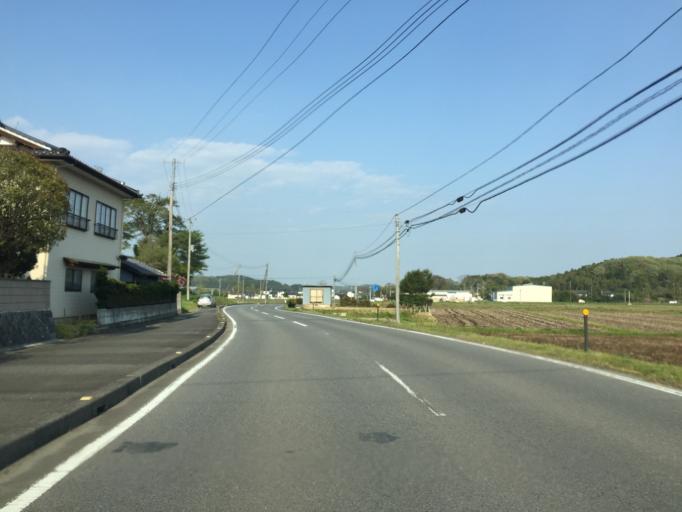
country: JP
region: Fukushima
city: Iwaki
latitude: 36.9568
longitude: 140.8240
